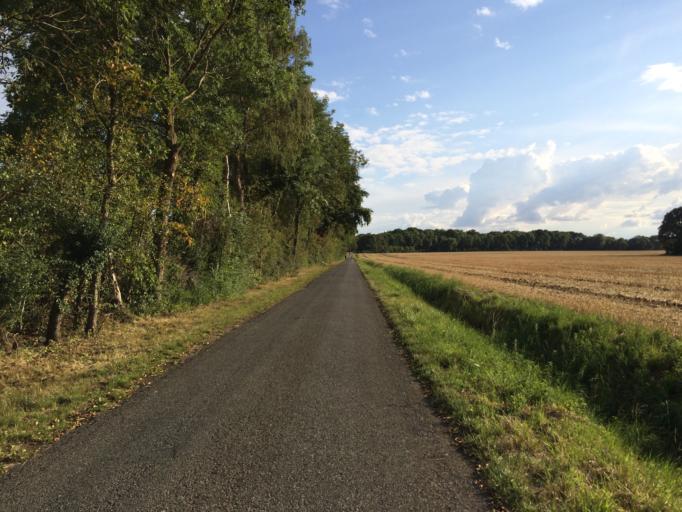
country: FR
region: Ile-de-France
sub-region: Departement de l'Essonne
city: Les Ulis
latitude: 48.6682
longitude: 2.1818
